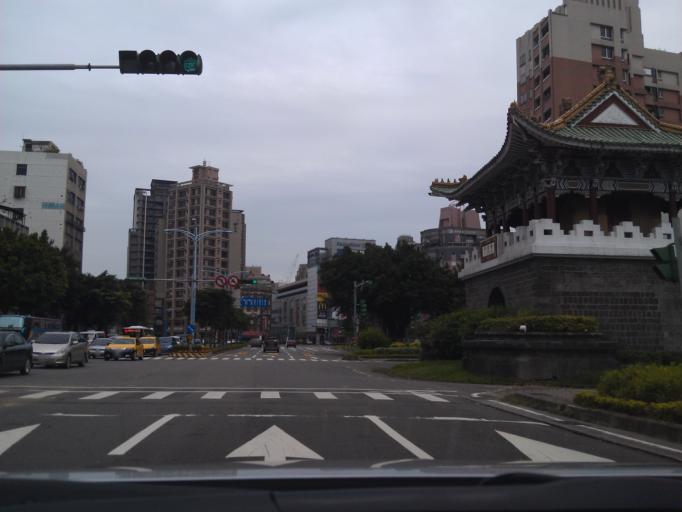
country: TW
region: Taipei
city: Taipei
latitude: 25.0367
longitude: 121.5083
